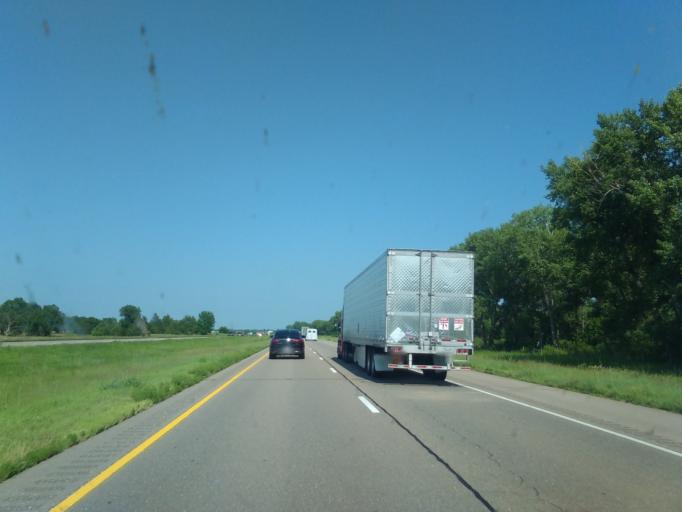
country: US
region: Nebraska
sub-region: Buffalo County
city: Gibbon
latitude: 40.6935
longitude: -98.8857
